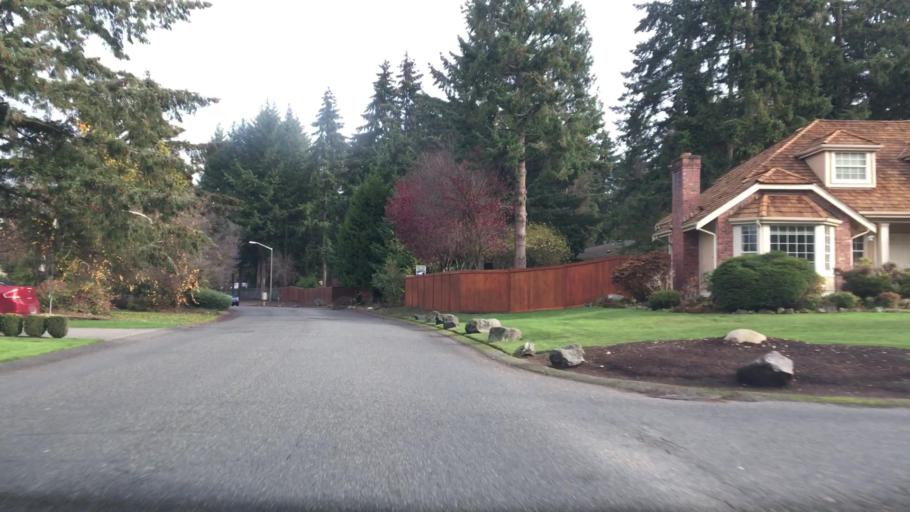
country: US
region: Washington
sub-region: Pierce County
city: South Hill
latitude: 47.1085
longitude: -122.3075
